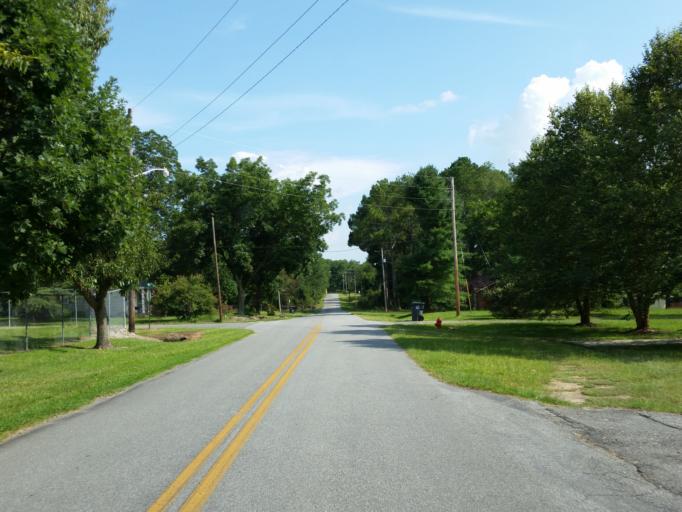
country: US
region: Georgia
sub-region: Crisp County
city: Cordele
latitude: 31.8315
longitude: -83.7419
